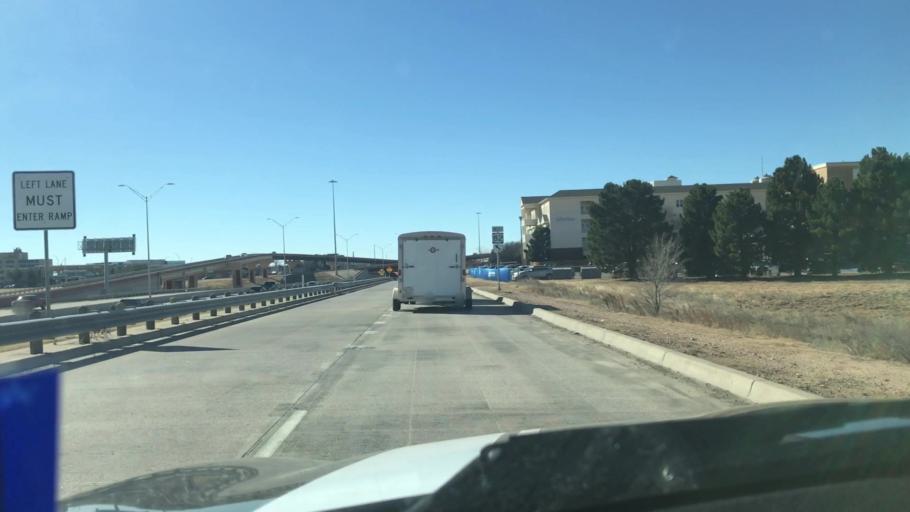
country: US
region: Texas
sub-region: Lubbock County
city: Lubbock
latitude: 33.5809
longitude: -101.8957
